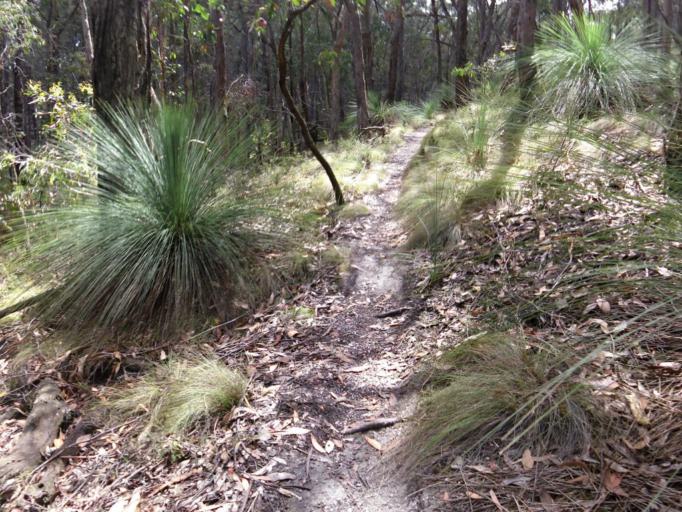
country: AU
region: Victoria
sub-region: Melton
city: Melton West
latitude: -37.4885
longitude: 144.5415
